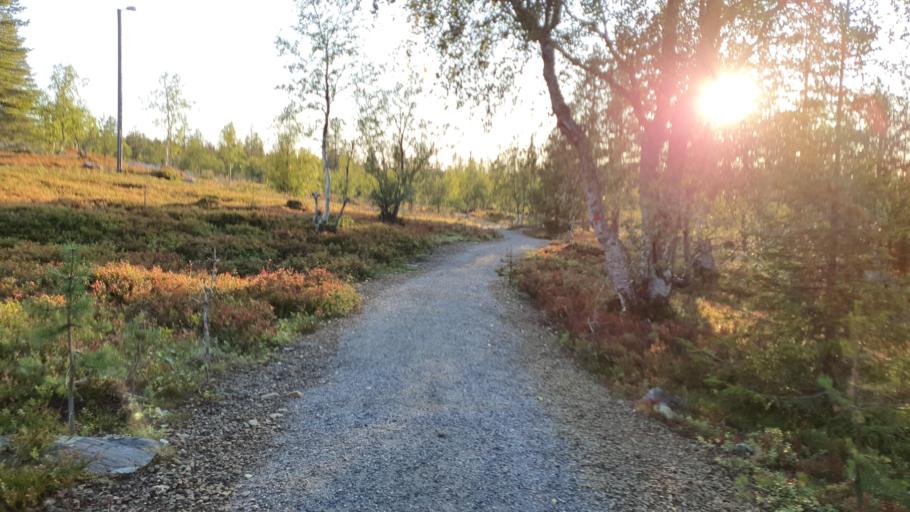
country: FI
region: Lapland
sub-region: Tunturi-Lappi
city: Kolari
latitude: 67.5822
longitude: 24.2225
